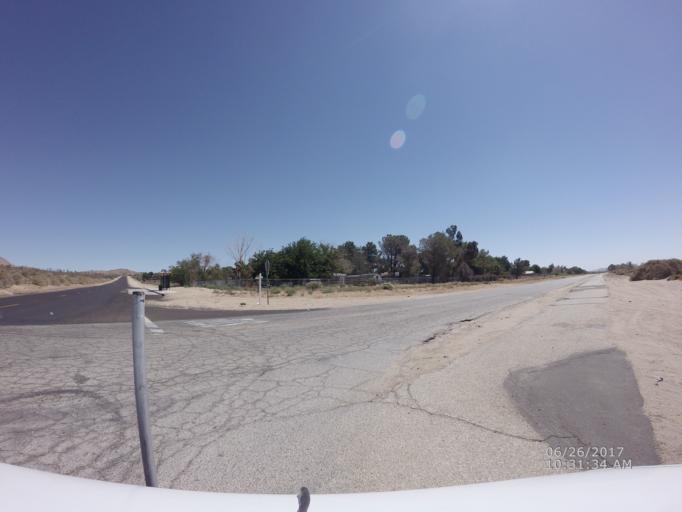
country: US
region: California
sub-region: Los Angeles County
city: Lake Los Angeles
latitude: 34.5871
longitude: -117.8444
